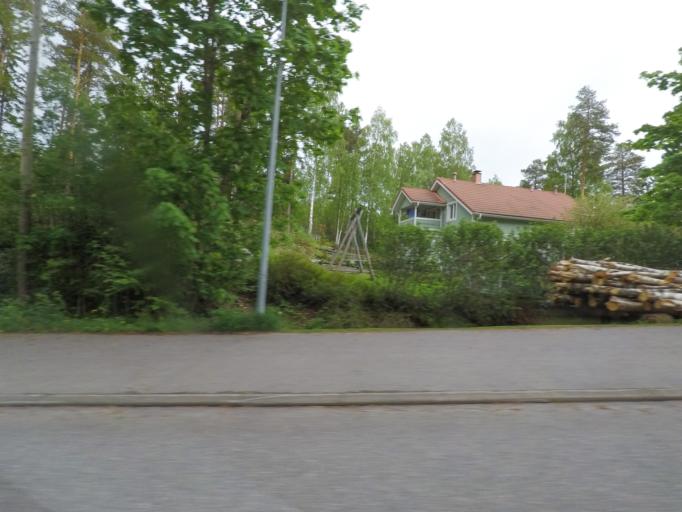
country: FI
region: Uusimaa
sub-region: Helsinki
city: Kirkkonummi
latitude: 60.1254
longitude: 24.4079
